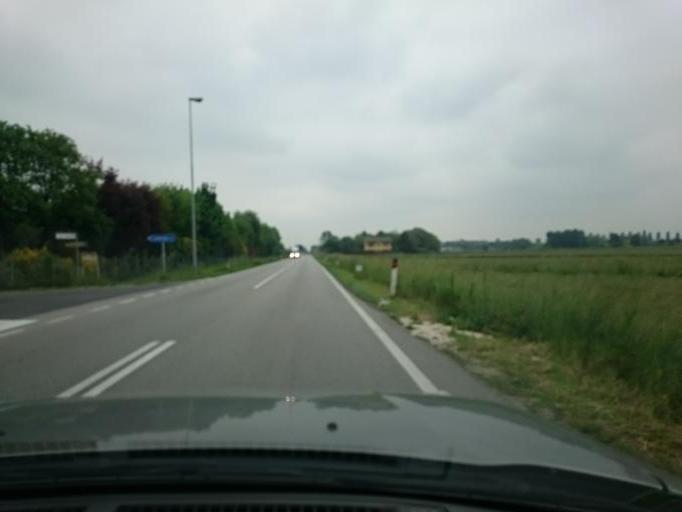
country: IT
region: Veneto
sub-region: Provincia di Padova
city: Masera di Padova
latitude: 45.2991
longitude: 11.8509
